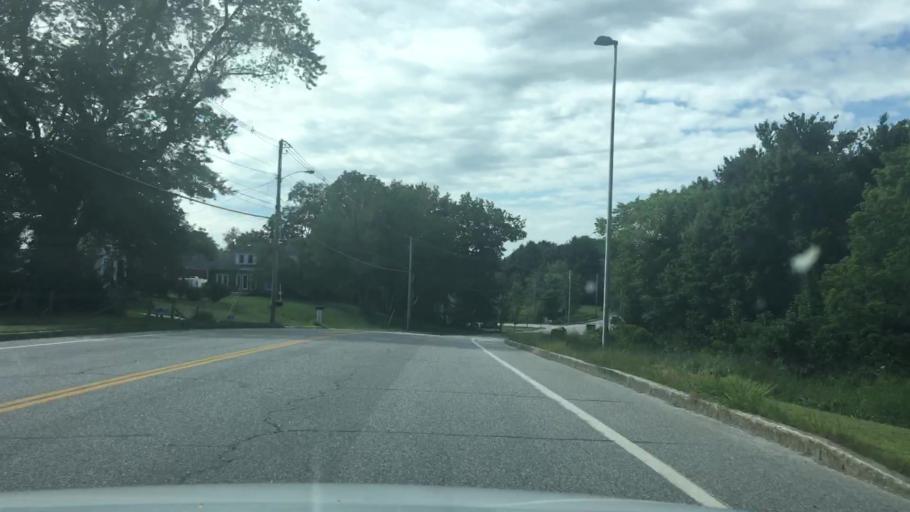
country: US
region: Maine
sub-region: Androscoggin County
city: Auburn
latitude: 44.1156
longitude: -70.2323
